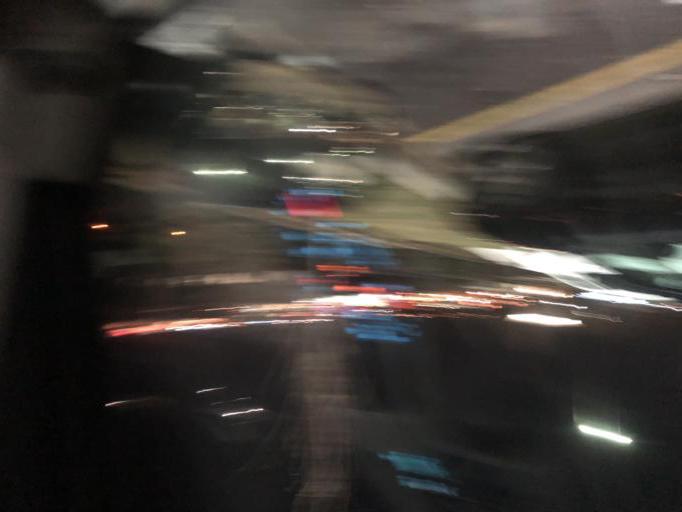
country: US
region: Colorado
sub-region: Arapahoe County
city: Centennial
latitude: 39.5915
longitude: -104.8603
